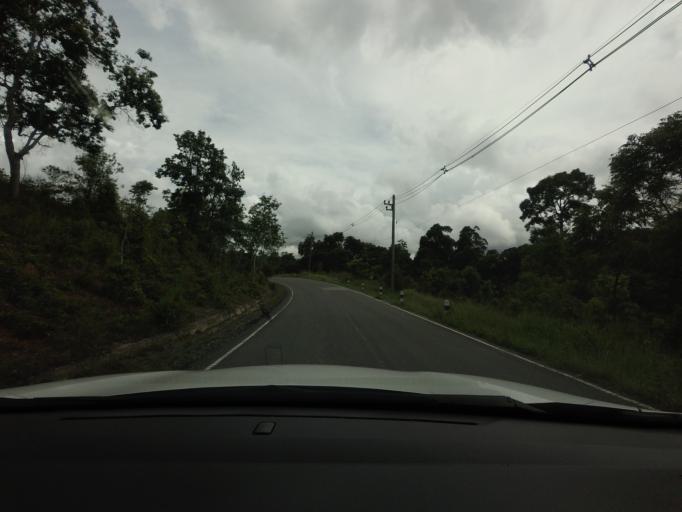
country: TH
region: Nakhon Nayok
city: Nakhon Nayok
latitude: 14.4270
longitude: 101.3696
